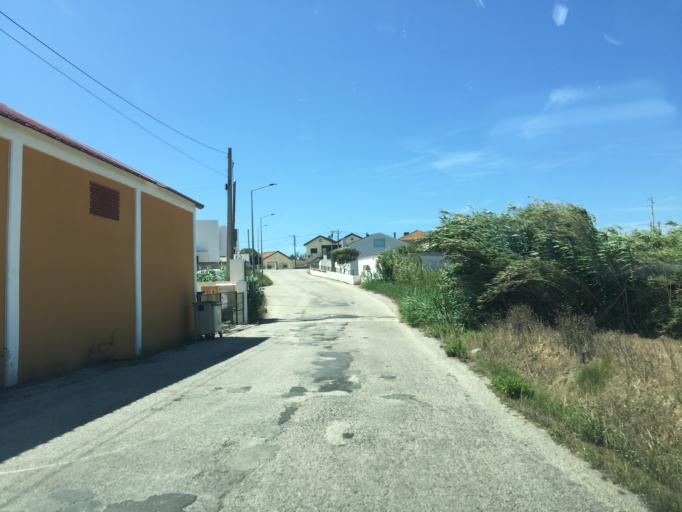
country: PT
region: Lisbon
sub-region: Lourinha
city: Lourinha
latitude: 39.2110
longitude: -9.3236
